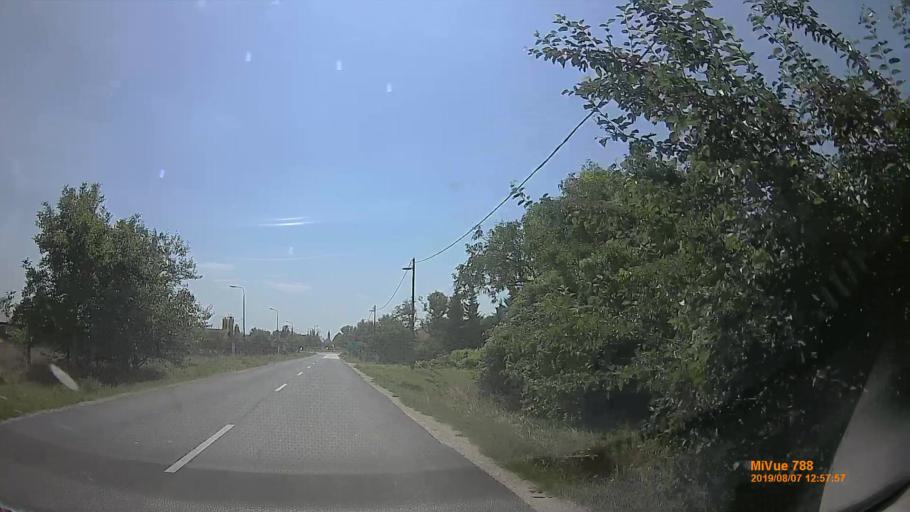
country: HU
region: Zala
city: Keszthely
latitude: 46.7843
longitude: 17.2536
